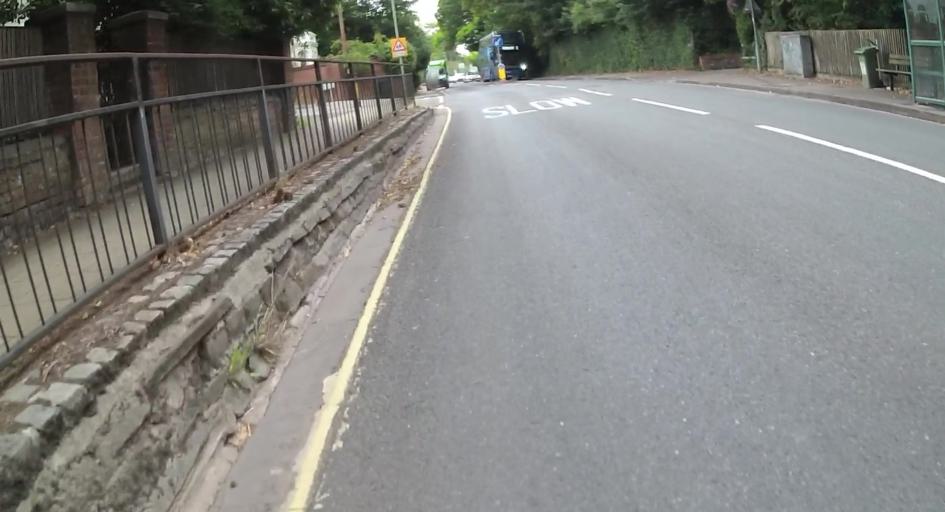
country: GB
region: England
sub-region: Hampshire
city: Winchester
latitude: 51.0524
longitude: -1.3216
